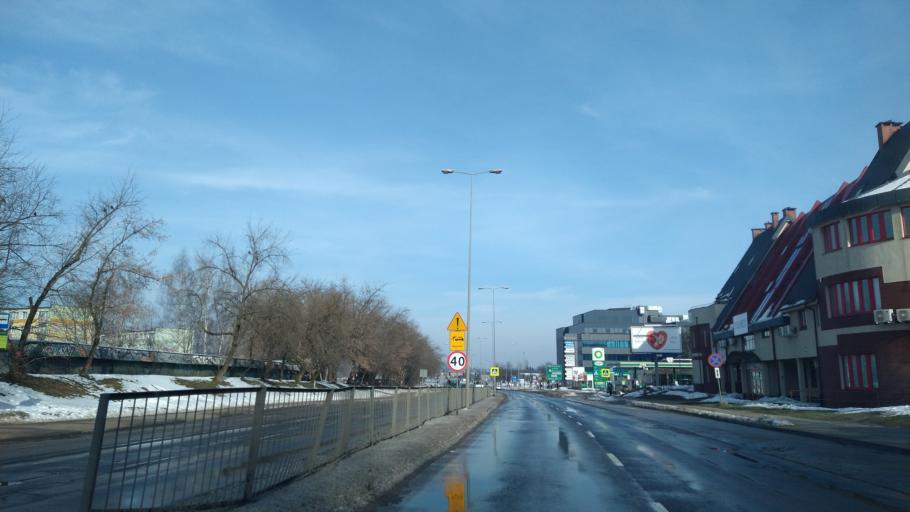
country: PL
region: Warmian-Masurian Voivodeship
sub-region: Powiat olsztynski
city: Olsztyn
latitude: 53.7685
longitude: 20.5071
